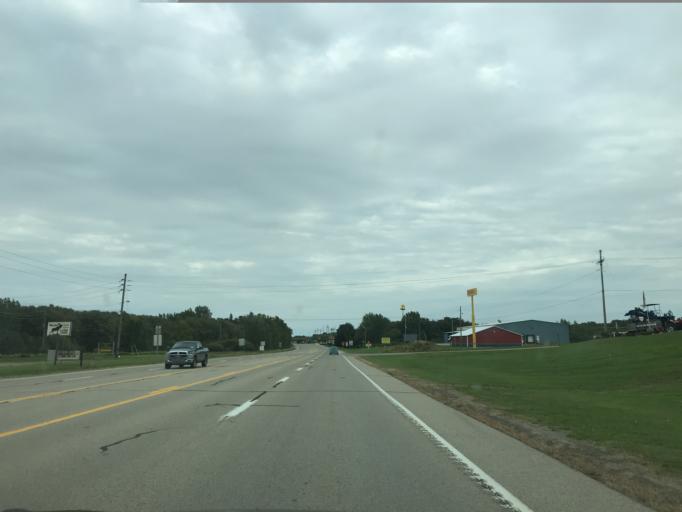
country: US
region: Pennsylvania
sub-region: Erie County
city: North East
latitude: 42.2301
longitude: -79.7891
